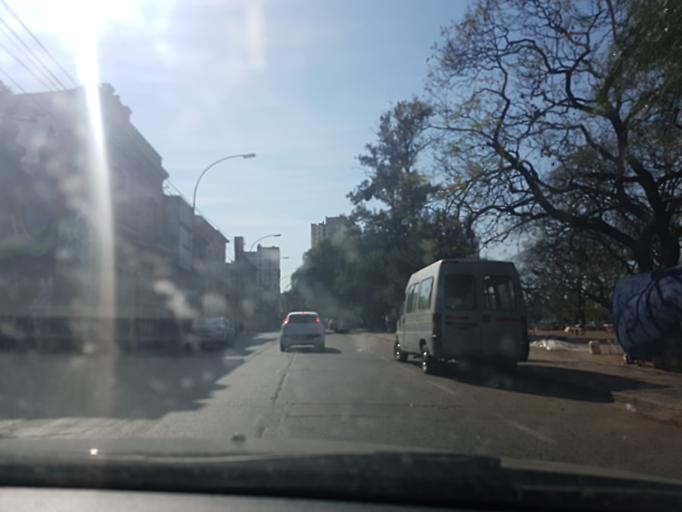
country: AR
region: Cordoba
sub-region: Departamento de Capital
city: Cordoba
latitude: -31.4051
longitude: -64.1847
